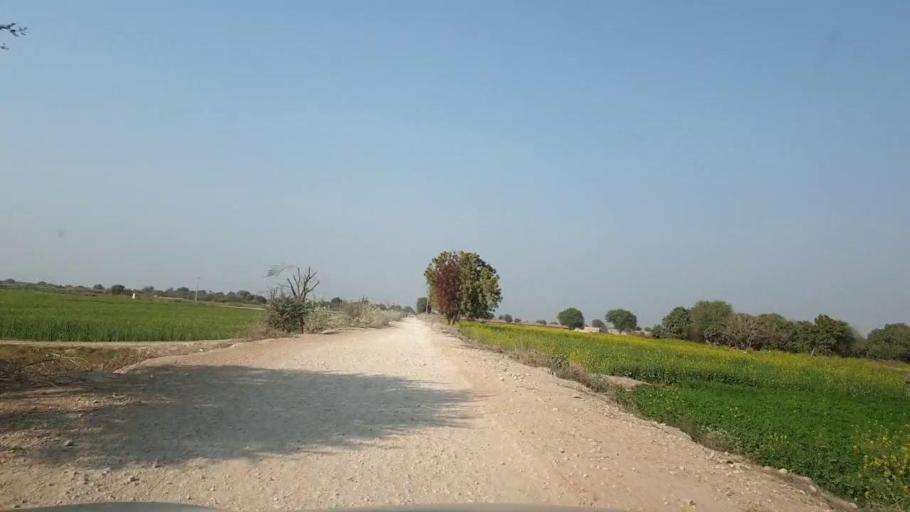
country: PK
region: Sindh
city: Tando Allahyar
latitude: 25.5640
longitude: 68.7941
